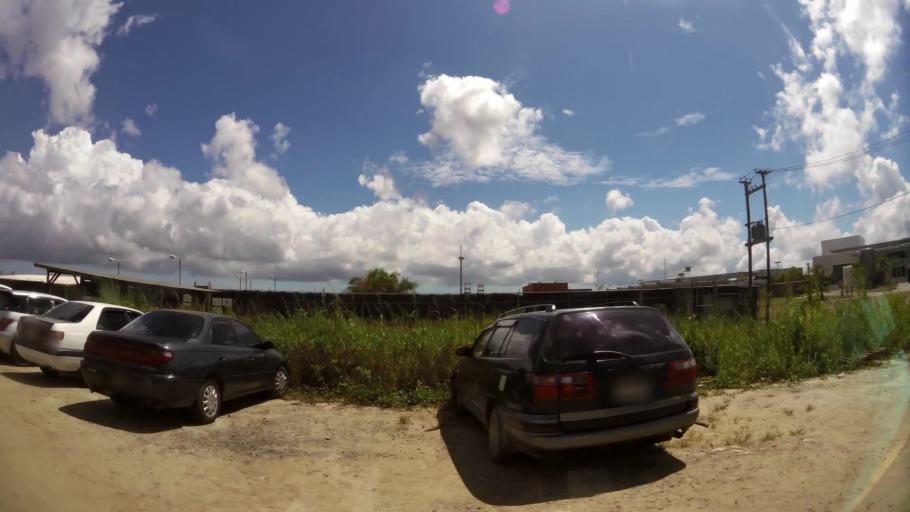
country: SR
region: Paramaribo
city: Paramaribo
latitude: 5.8643
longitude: -55.1286
